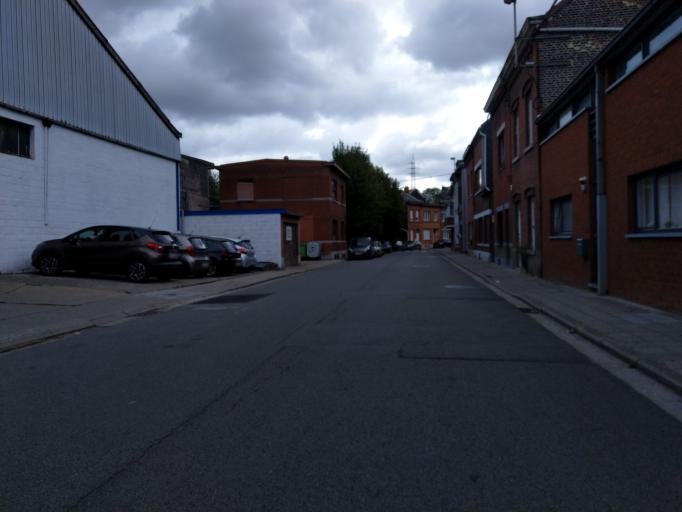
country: BE
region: Wallonia
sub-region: Province de Liege
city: Saint-Nicolas
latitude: 50.6200
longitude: 5.5236
